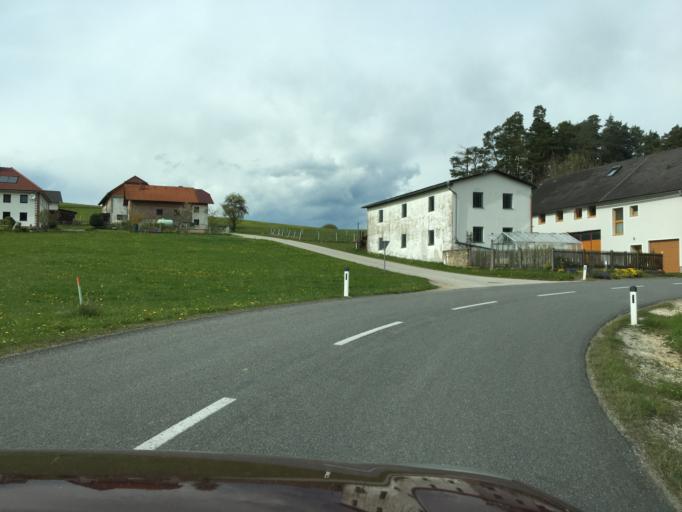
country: AT
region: Upper Austria
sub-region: Politischer Bezirk Urfahr-Umgebung
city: Reichenthal
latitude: 48.5133
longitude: 14.4320
